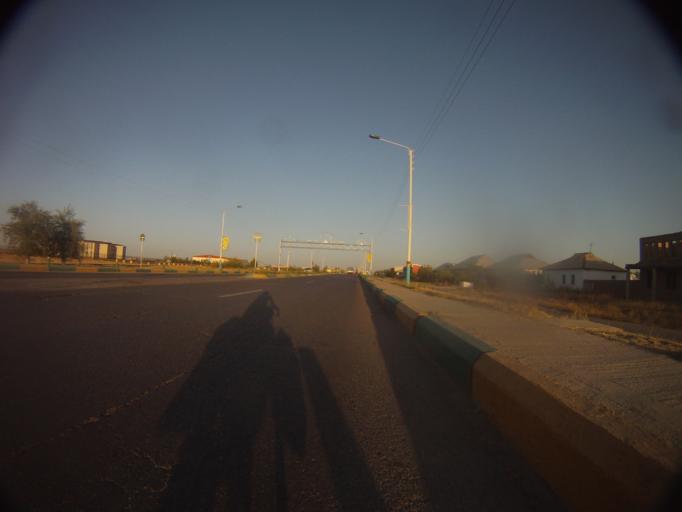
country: KZ
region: Ongtustik Qazaqstan
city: Turkestan
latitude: 43.2867
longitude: 68.3024
